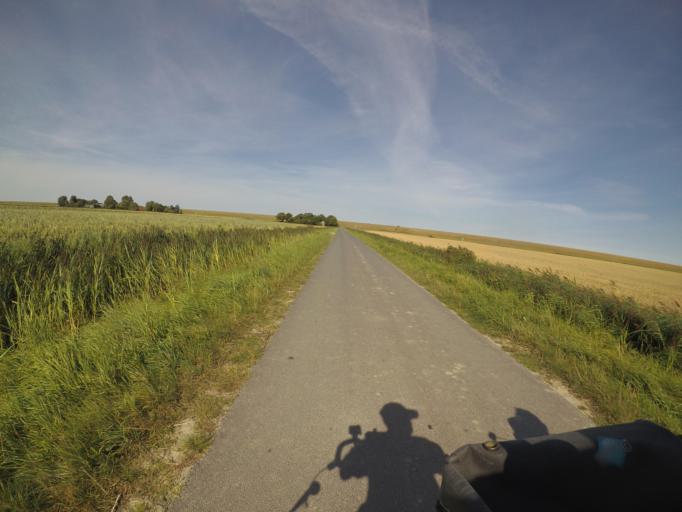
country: NL
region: Friesland
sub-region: Gemeente Ferwerderadiel
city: Marrum
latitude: 53.3413
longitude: 5.7998
